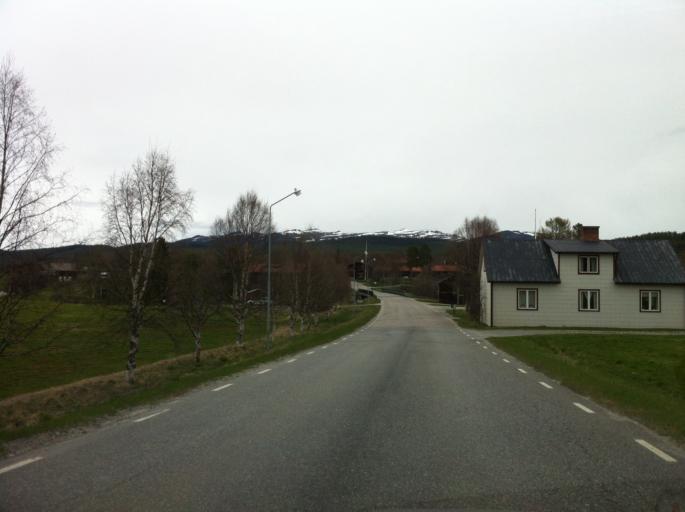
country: NO
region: Hedmark
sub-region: Engerdal
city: Engerdal
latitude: 62.5252
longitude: 12.5922
